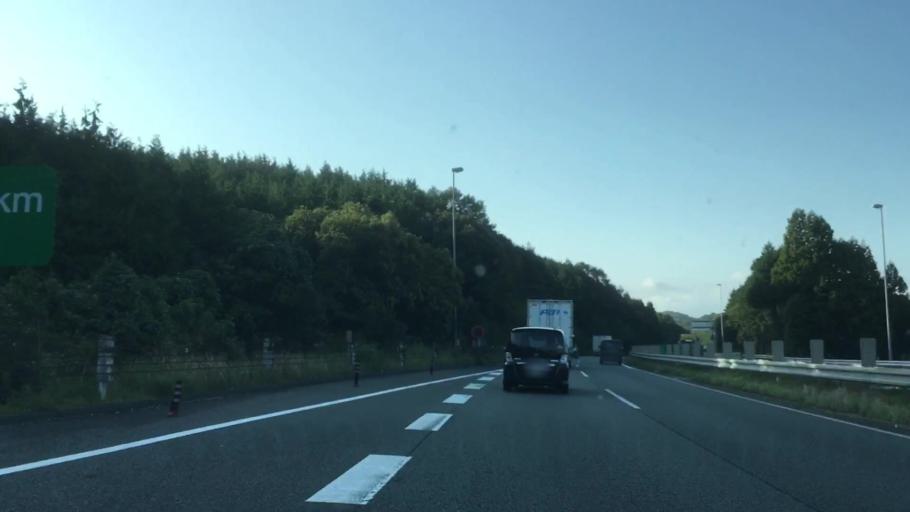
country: JP
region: Yamaguchi
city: Ogori-shimogo
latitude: 34.1554
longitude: 131.3341
